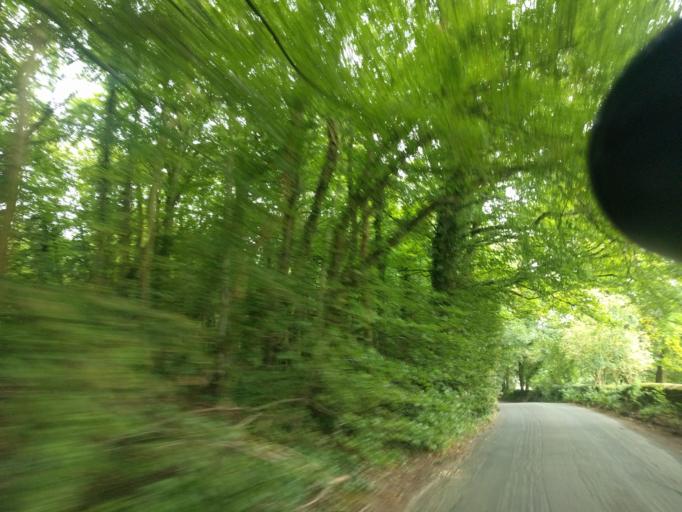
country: GB
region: England
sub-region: Wiltshire
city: Box
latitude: 51.4199
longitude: -2.2412
